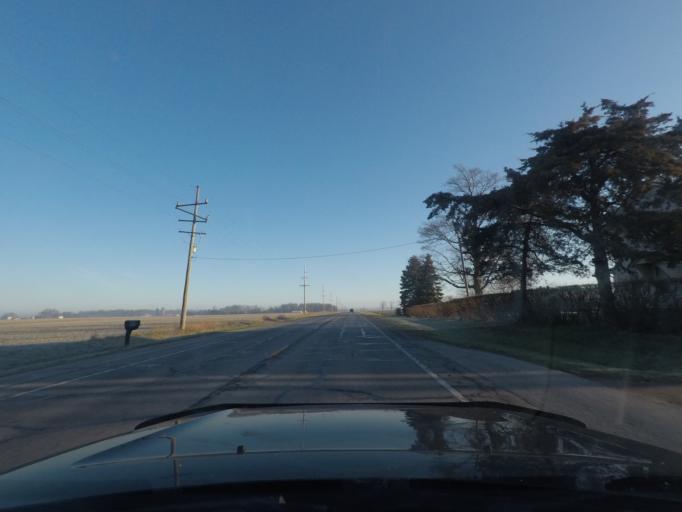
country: US
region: Indiana
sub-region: Elkhart County
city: Wakarusa
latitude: 41.5010
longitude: -86.0020
